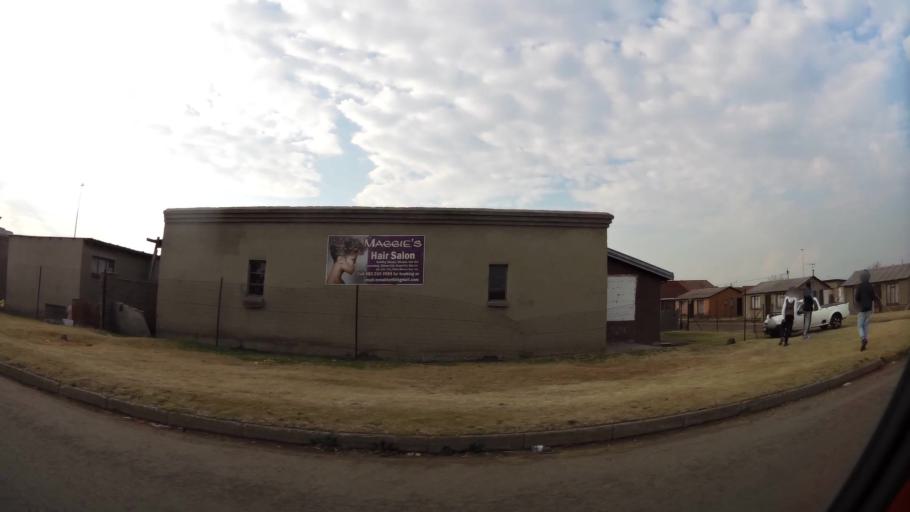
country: ZA
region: Gauteng
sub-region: Sedibeng District Municipality
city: Vanderbijlpark
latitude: -26.6906
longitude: 27.8791
